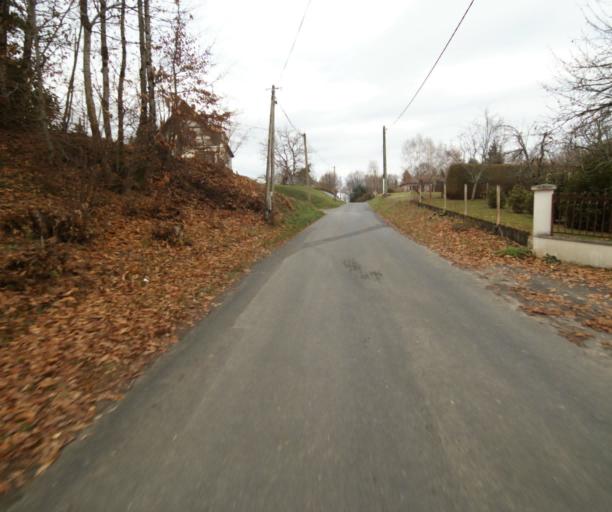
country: FR
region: Limousin
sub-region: Departement de la Correze
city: Sainte-Fortunade
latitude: 45.2267
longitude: 1.7649
